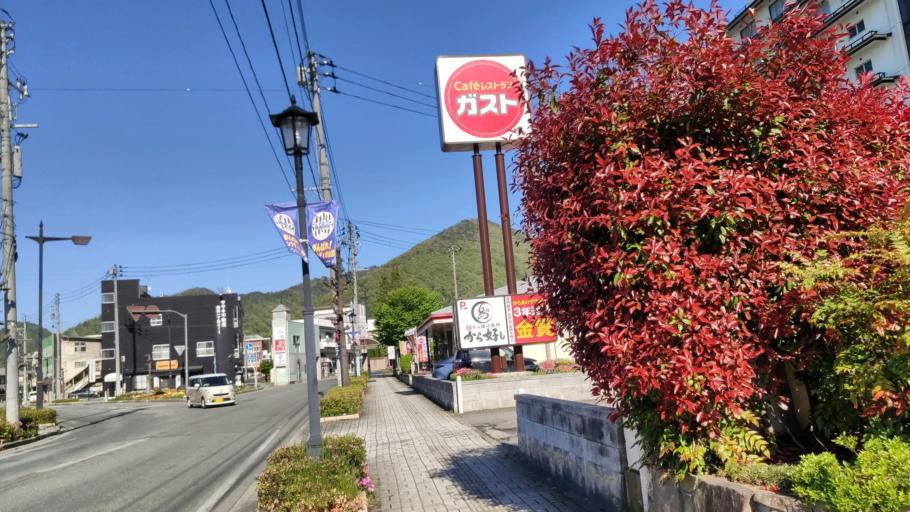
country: JP
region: Yamagata
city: Tendo
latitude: 38.3598
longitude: 140.3820
